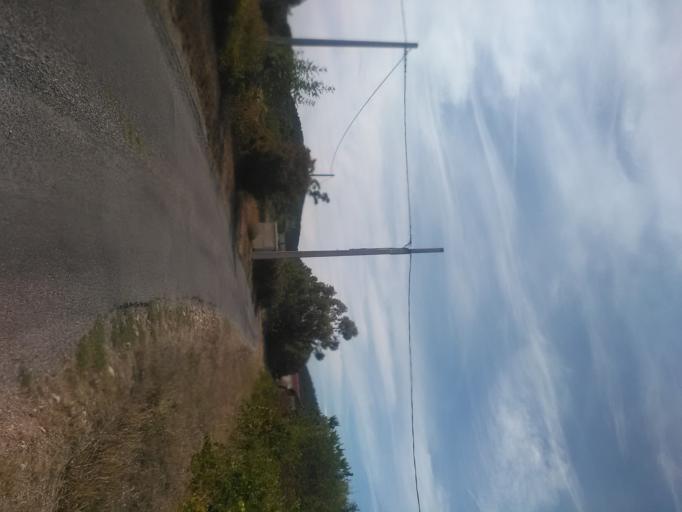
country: FR
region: Provence-Alpes-Cote d'Azur
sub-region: Departement des Alpes-de-Haute-Provence
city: Manosque
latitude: 43.8338
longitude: 5.8230
